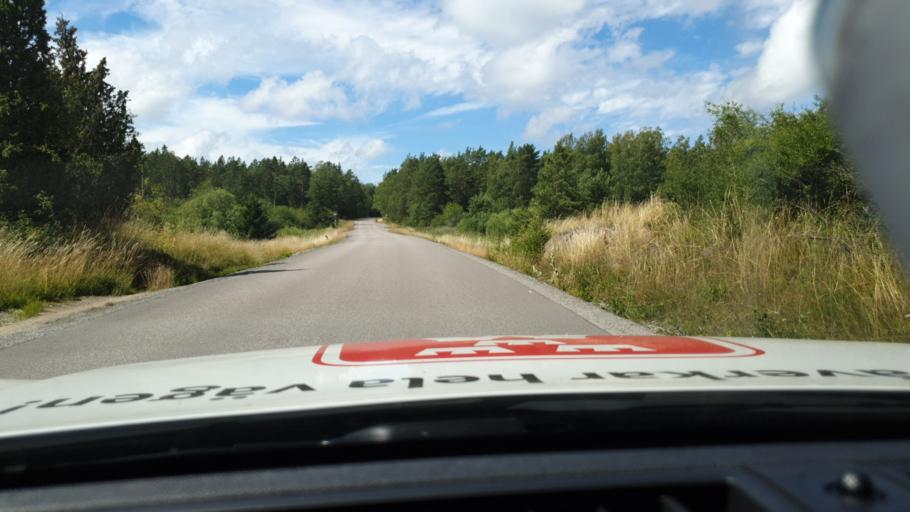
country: SE
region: Stockholm
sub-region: Haninge Kommun
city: Jordbro
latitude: 59.0251
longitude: 18.1701
